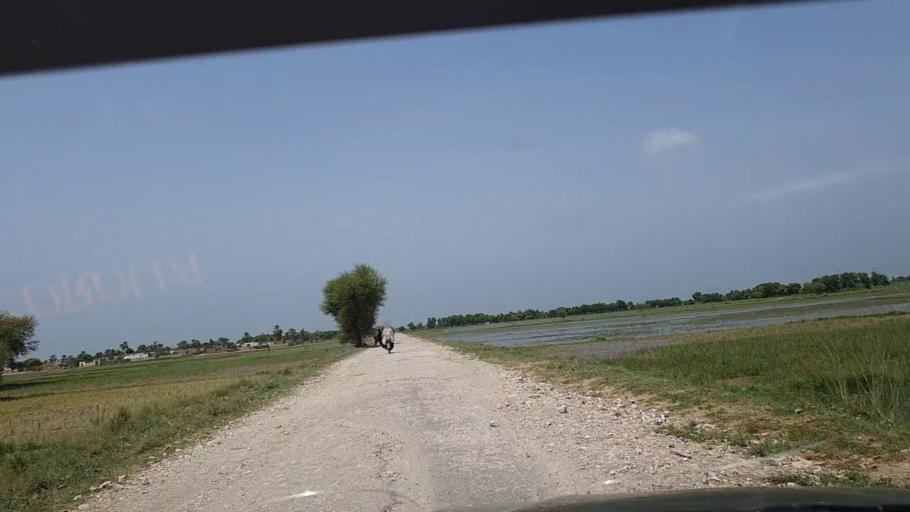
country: PK
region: Sindh
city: Khanpur
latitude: 27.8203
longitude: 69.4443
